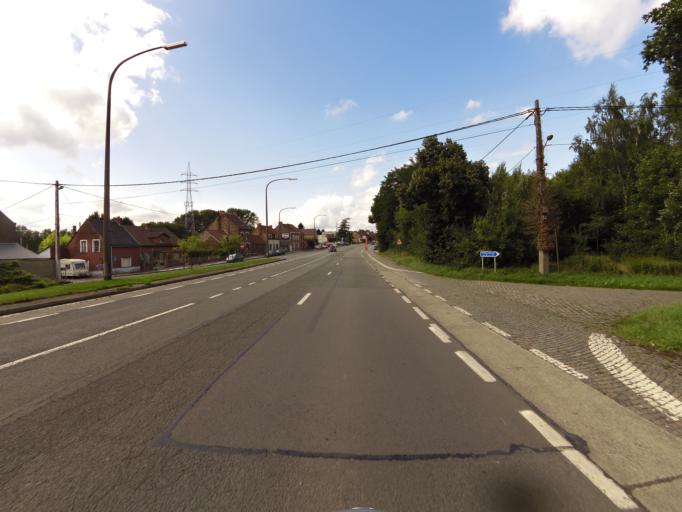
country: BE
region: Wallonia
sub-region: Province du Hainaut
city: Saint-Ghislain
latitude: 50.4767
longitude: 3.8458
